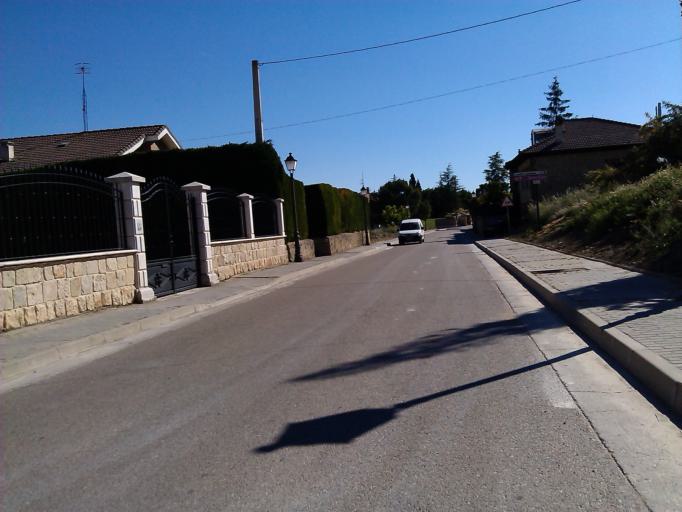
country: ES
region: Castille and Leon
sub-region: Provincia de Burgos
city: Villaquiran de la Puebla
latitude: 42.2884
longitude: -4.1339
